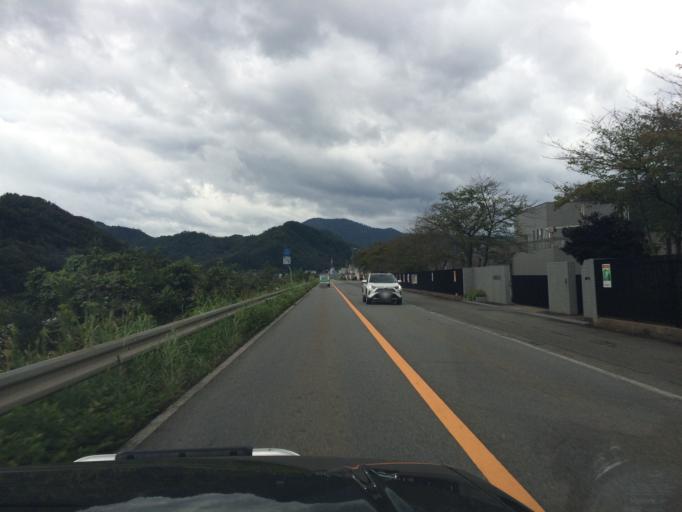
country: JP
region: Hyogo
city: Toyooka
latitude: 35.4147
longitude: 134.7828
